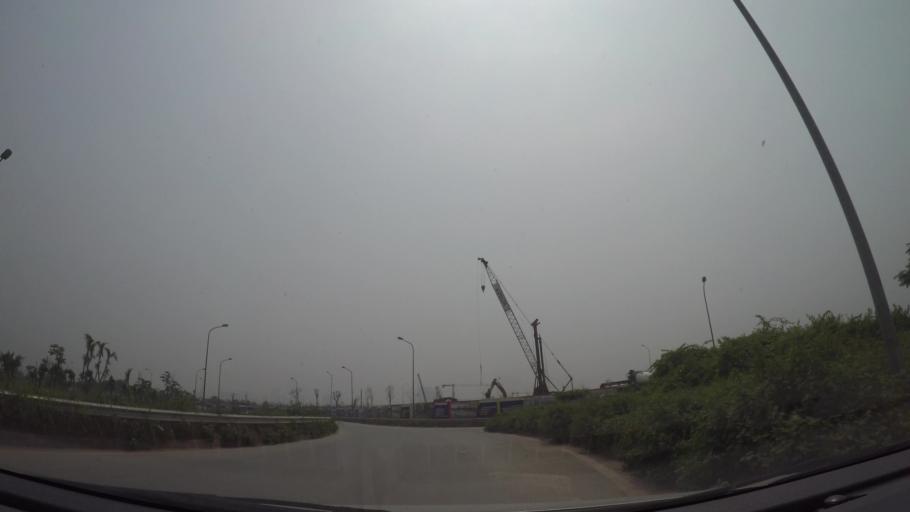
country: VN
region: Ha Noi
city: Cau Dien
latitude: 21.0066
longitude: 105.7484
